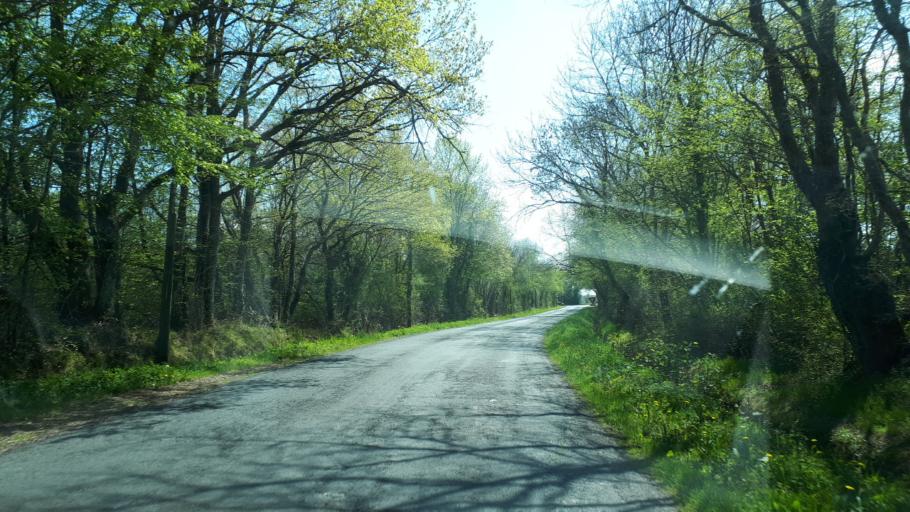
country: FR
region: Centre
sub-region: Departement du Cher
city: Henrichemont
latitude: 47.2998
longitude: 2.5104
